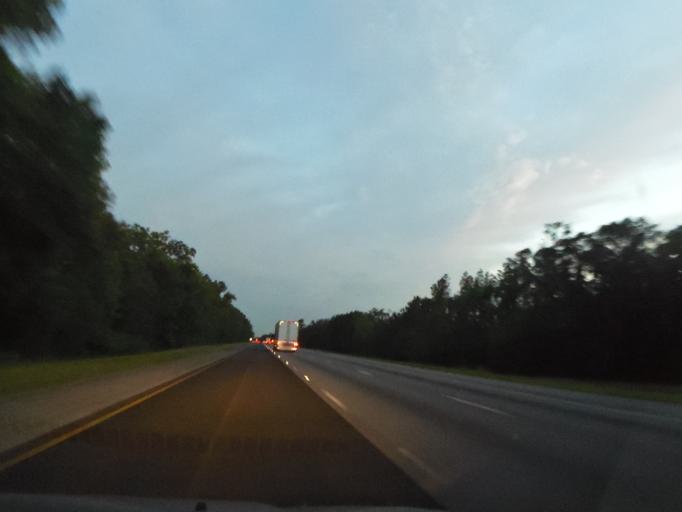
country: US
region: Georgia
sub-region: Liberty County
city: Midway
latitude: 31.7114
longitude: -81.3906
